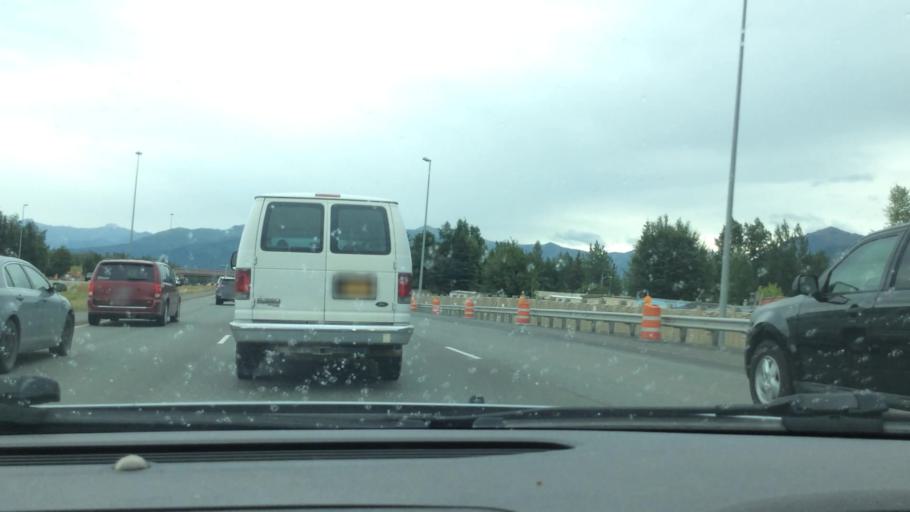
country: US
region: Alaska
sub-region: Anchorage Municipality
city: Elmendorf Air Force Base
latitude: 61.2249
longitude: -149.7437
